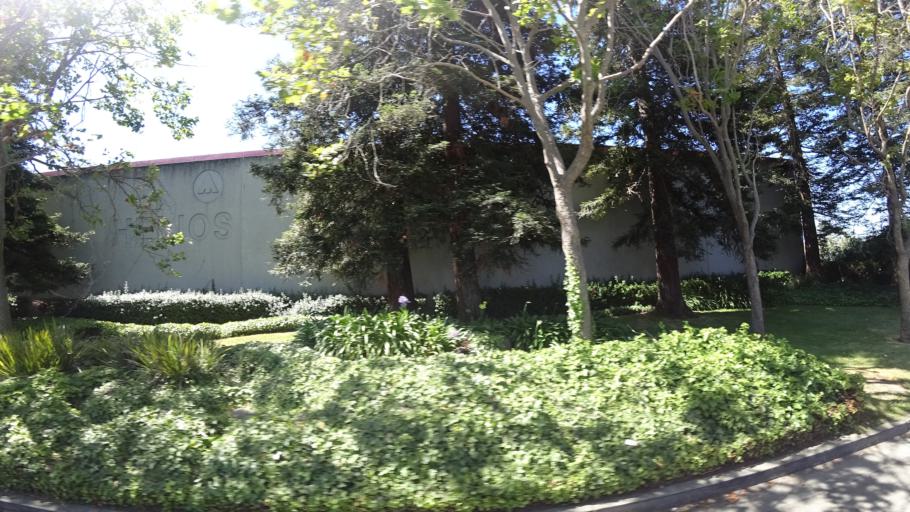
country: US
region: California
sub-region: Alameda County
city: San Lorenzo
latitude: 37.6542
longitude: -122.1333
